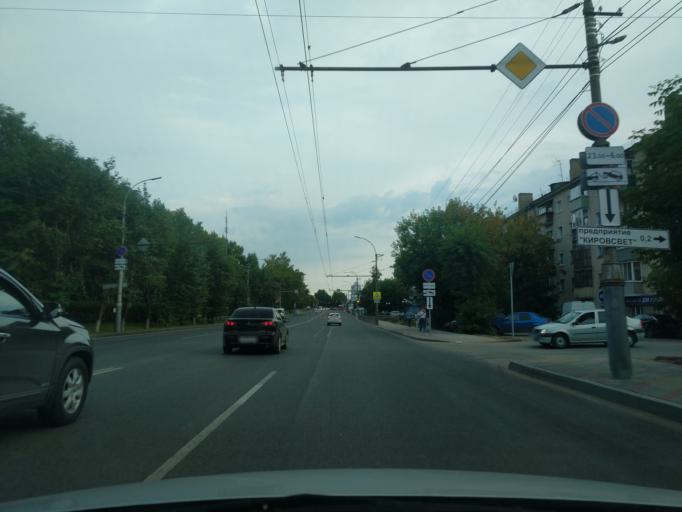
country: RU
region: Kirov
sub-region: Kirovo-Chepetskiy Rayon
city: Kirov
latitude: 58.6183
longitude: 49.6562
